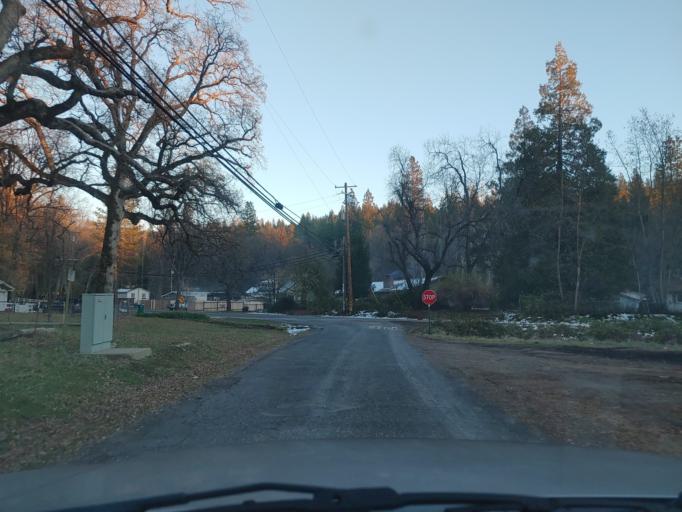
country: US
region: California
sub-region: Tuolumne County
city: Twain Harte
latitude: 38.0262
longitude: -120.2540
